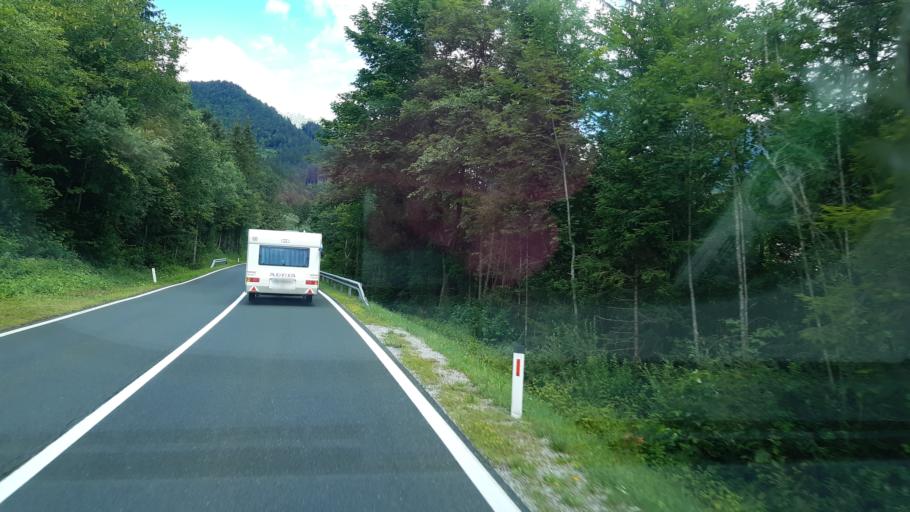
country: SI
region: Trzic
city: Trzic
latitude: 46.3850
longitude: 14.2929
